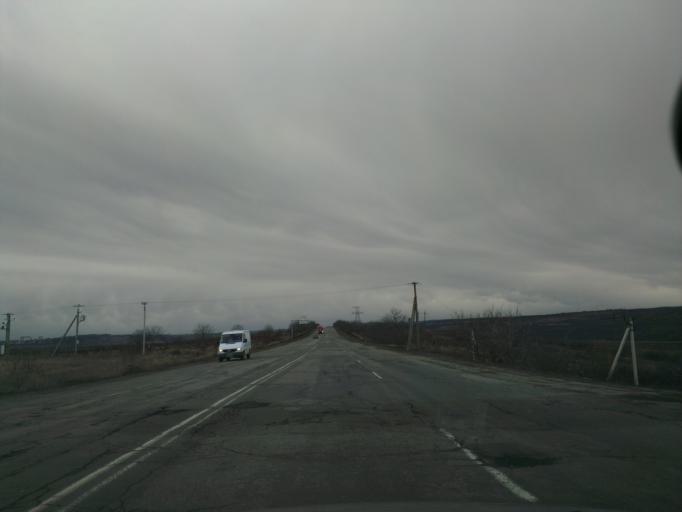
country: MD
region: Chisinau
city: Vatra
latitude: 47.0116
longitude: 28.7249
